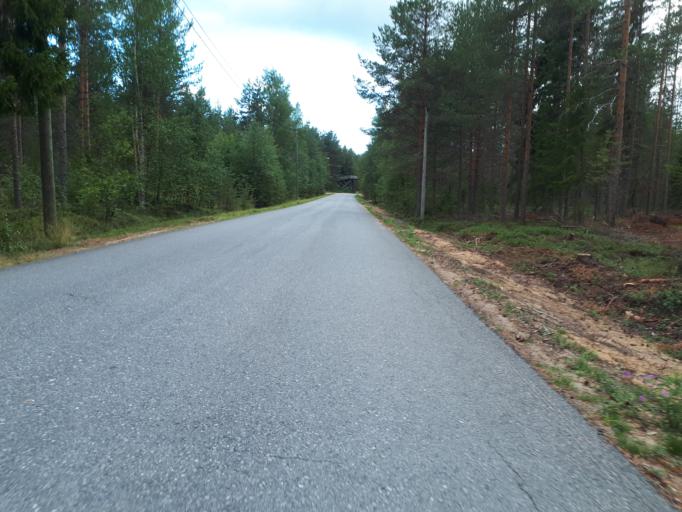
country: FI
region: Northern Ostrobothnia
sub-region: Oulunkaari
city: Ii
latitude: 65.3293
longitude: 25.3950
